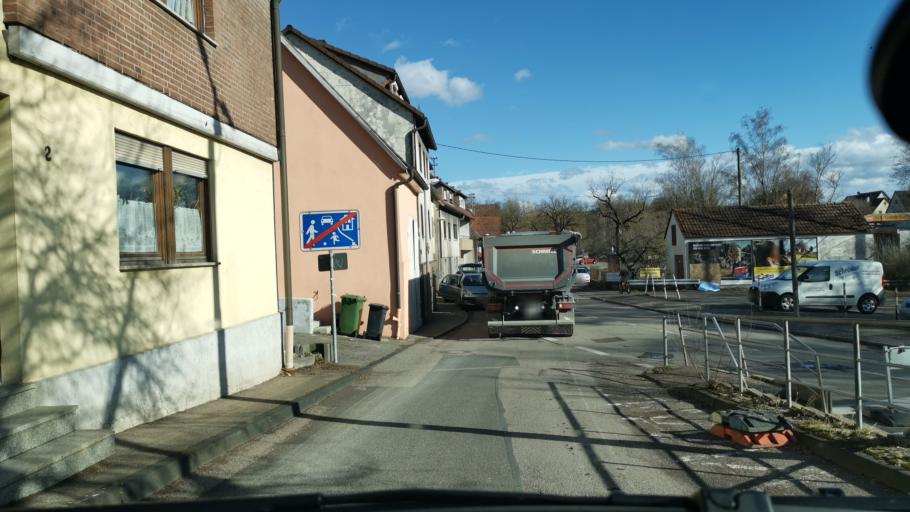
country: DE
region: Baden-Wuerttemberg
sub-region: Regierungsbezirk Stuttgart
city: Ehningen
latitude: 48.6981
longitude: 8.9394
